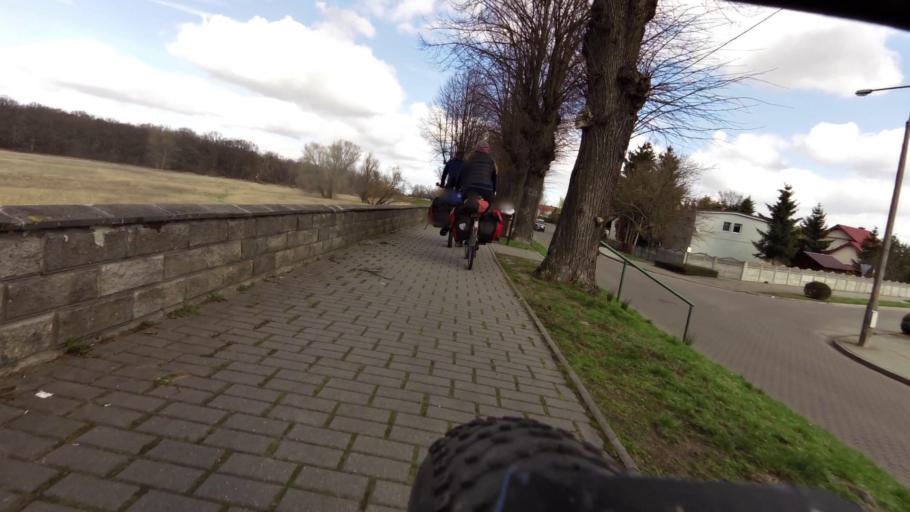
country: PL
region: Lubusz
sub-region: Powiat slubicki
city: Slubice
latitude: 52.3591
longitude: 14.5593
